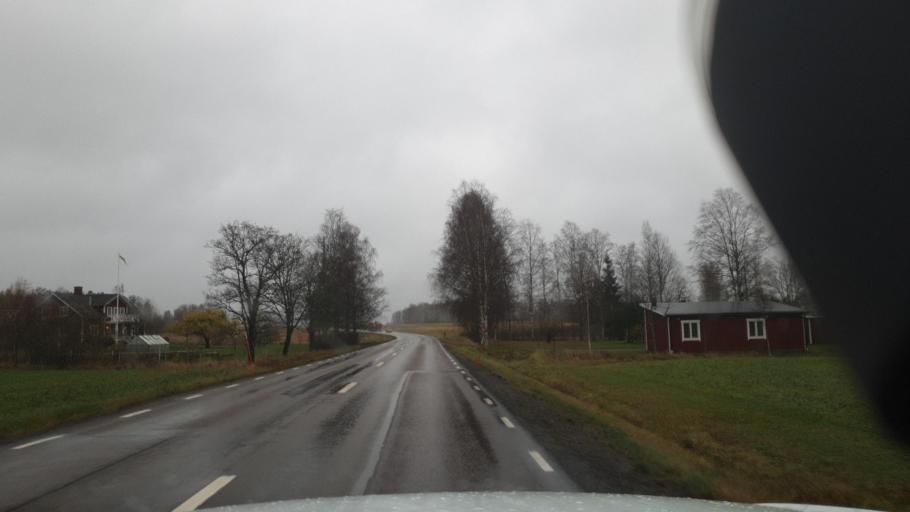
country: SE
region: Vaermland
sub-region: Sunne Kommun
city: Sunne
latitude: 59.7291
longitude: 13.1238
